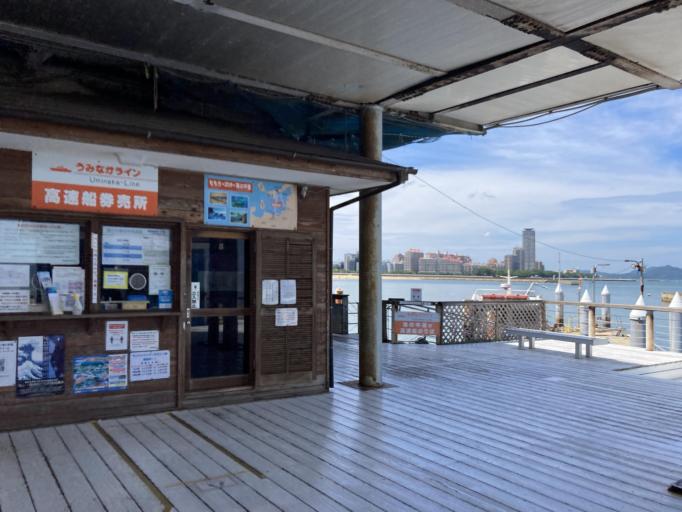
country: JP
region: Fukuoka
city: Fukuoka-shi
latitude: 33.5959
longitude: 130.3511
